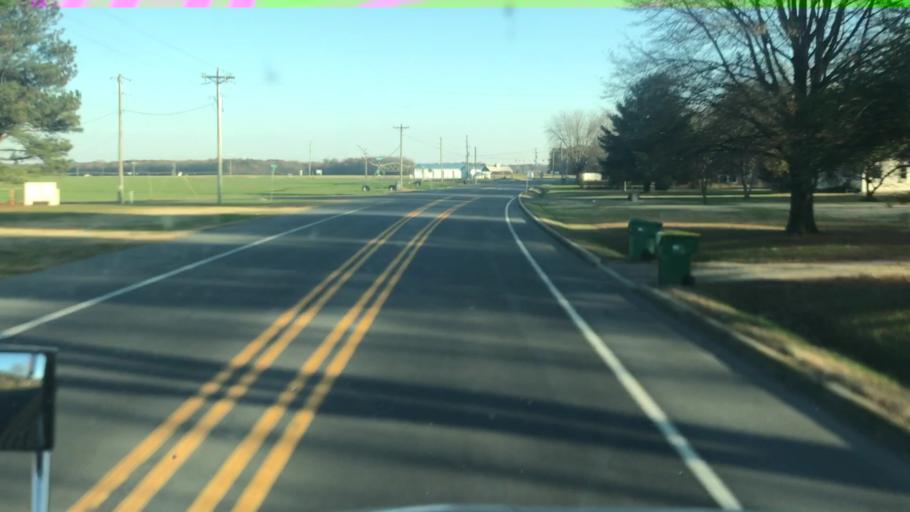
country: US
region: Delaware
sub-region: Sussex County
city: Bridgeville
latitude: 38.7818
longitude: -75.6696
